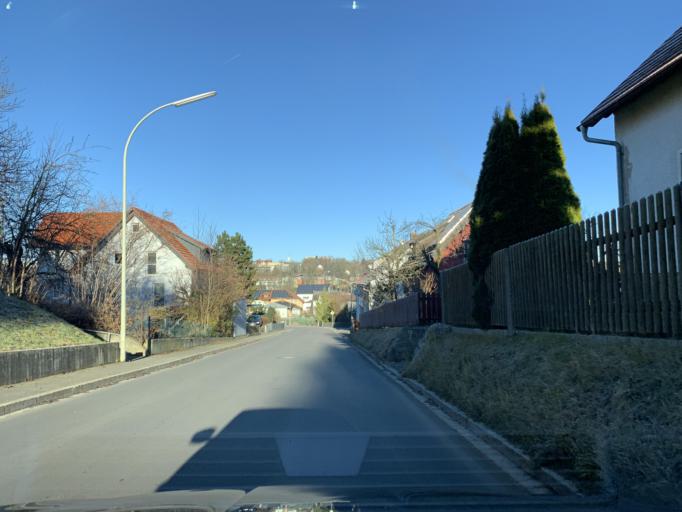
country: DE
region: Bavaria
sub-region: Upper Palatinate
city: Oberviechtach
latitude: 49.4539
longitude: 12.4187
